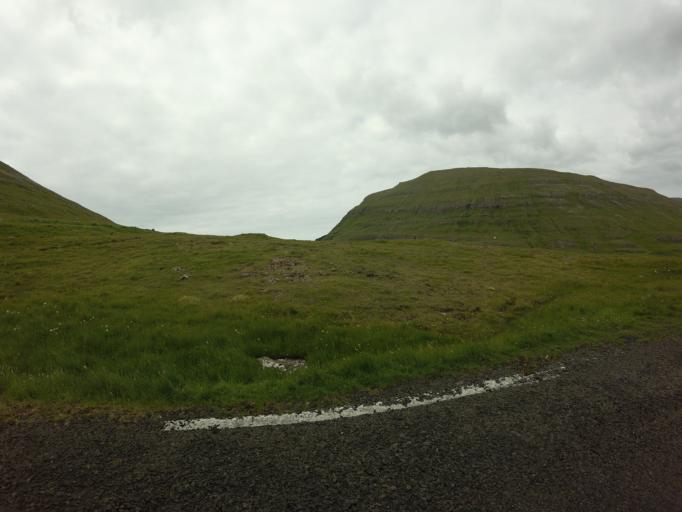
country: FO
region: Suduroy
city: Vagur
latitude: 61.4416
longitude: -6.7765
